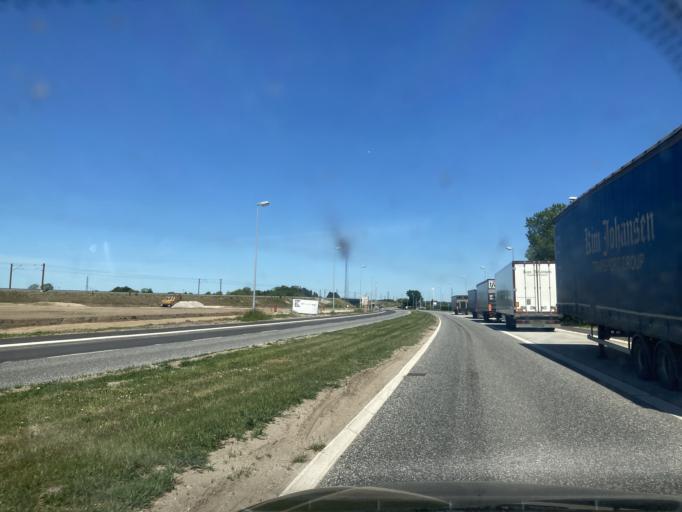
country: DK
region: Capital Region
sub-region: Ishoj Kommune
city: Ishoj
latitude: 55.6191
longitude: 12.3183
